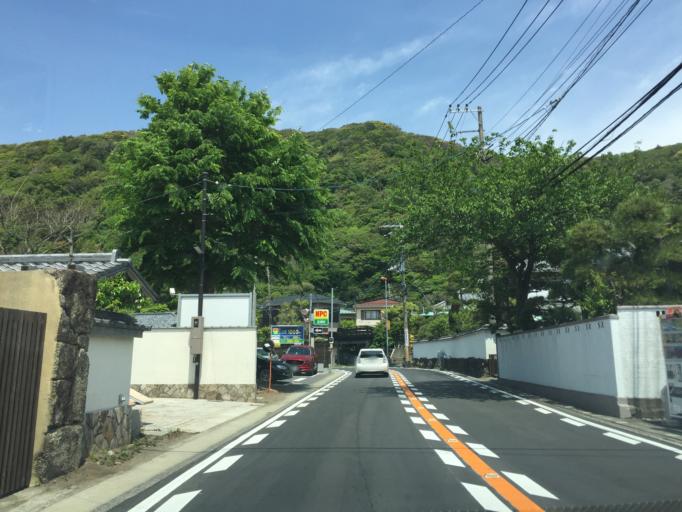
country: JP
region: Kanagawa
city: Hayama
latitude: 35.2649
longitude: 139.5779
